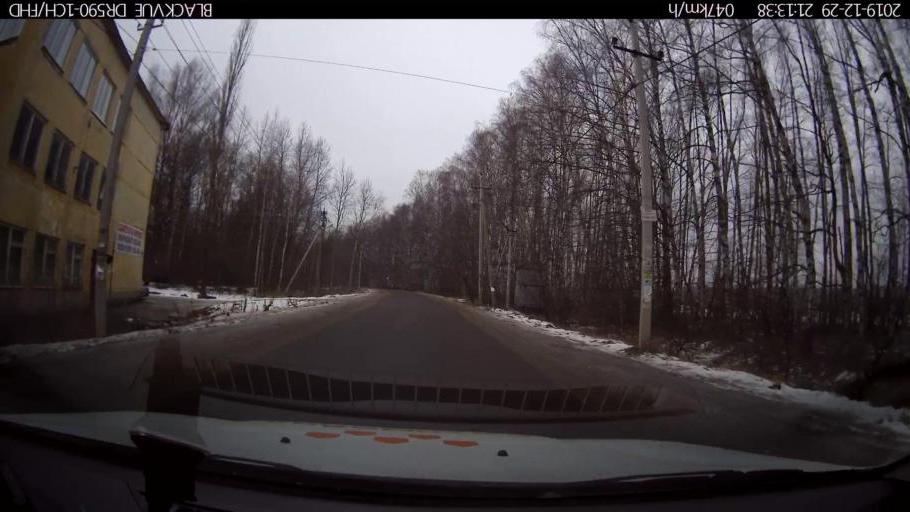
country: RU
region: Nizjnij Novgorod
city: Afonino
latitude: 56.2175
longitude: 44.0356
